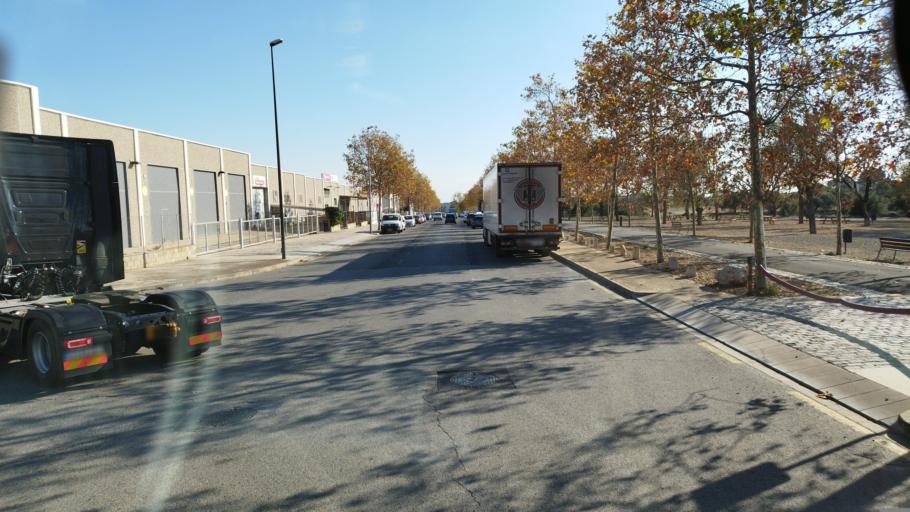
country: ES
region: Catalonia
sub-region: Provincia de Tarragona
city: Reus
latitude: 41.1564
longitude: 1.0767
